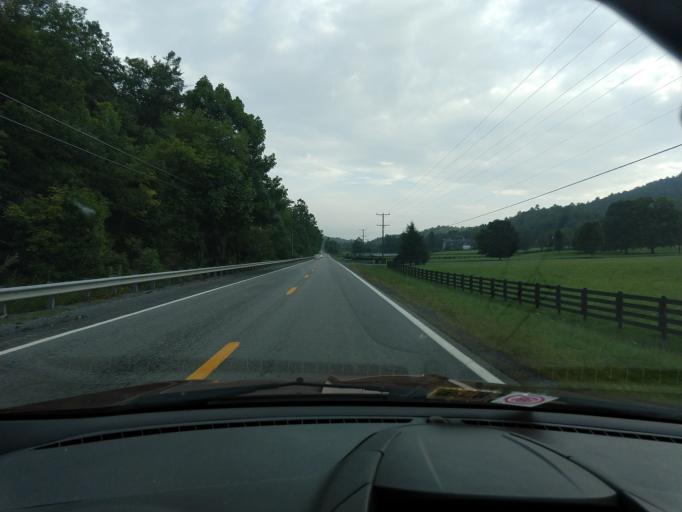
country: US
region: West Virginia
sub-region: Greenbrier County
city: White Sulphur Springs
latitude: 37.8467
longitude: -80.2514
